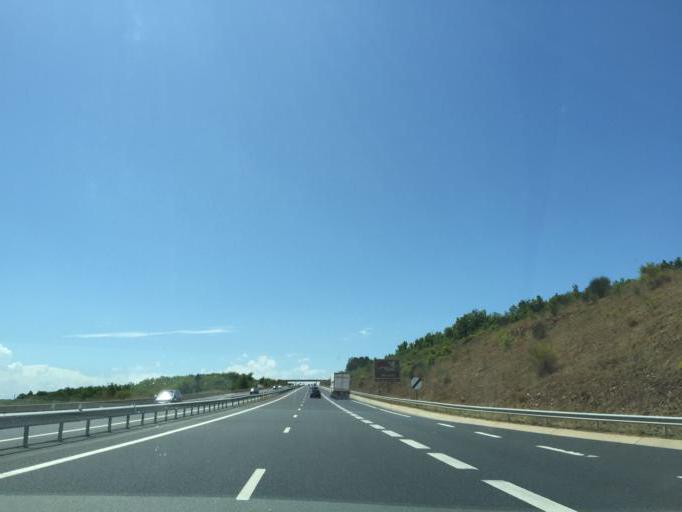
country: FR
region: Midi-Pyrenees
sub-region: Departement de l'Aveyron
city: Millau
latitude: 44.1937
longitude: 3.0621
